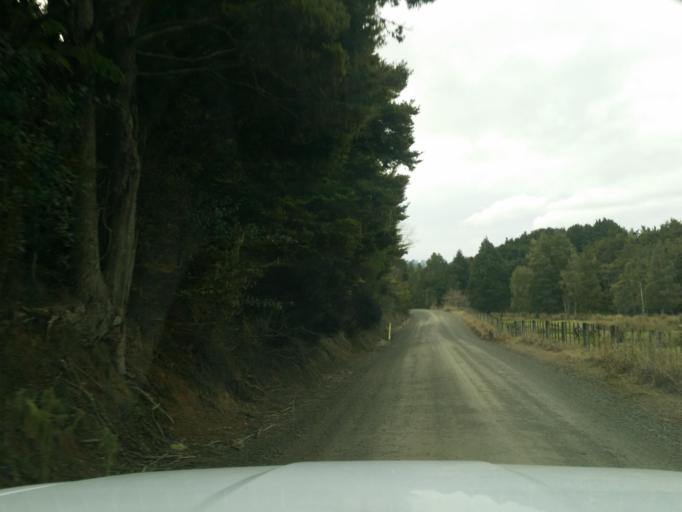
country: NZ
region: Northland
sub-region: Kaipara District
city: Dargaville
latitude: -35.7510
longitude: 173.9159
